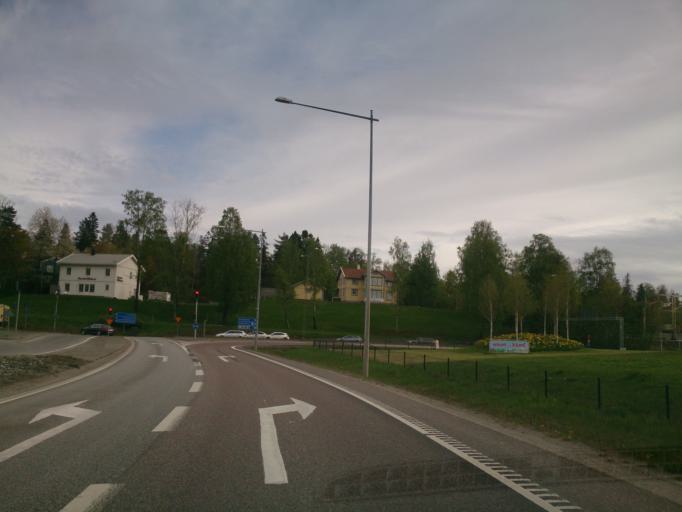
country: SE
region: Stockholm
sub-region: Haninge Kommun
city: Haninge
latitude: 59.1789
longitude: 18.1534
